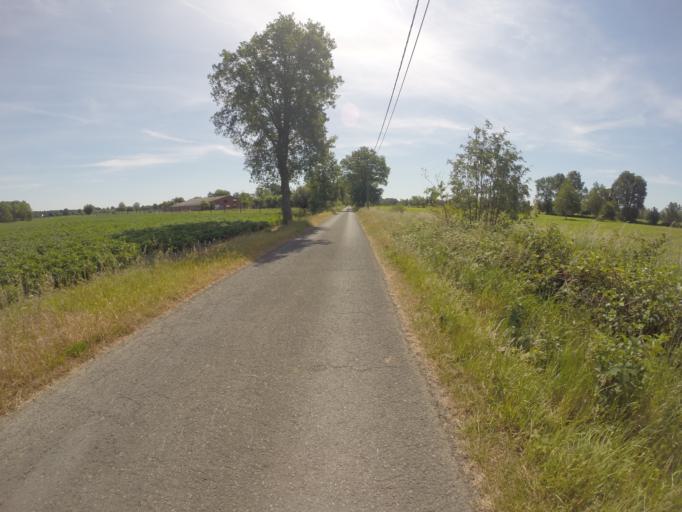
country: BE
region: Flanders
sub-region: Provincie West-Vlaanderen
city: Beernem
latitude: 51.1480
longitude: 3.3628
